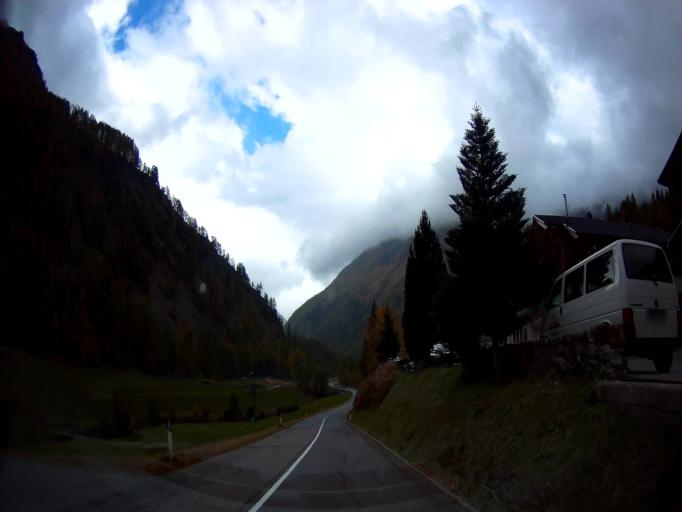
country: IT
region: Trentino-Alto Adige
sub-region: Bolzano
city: Senales
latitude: 46.7343
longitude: 10.8026
